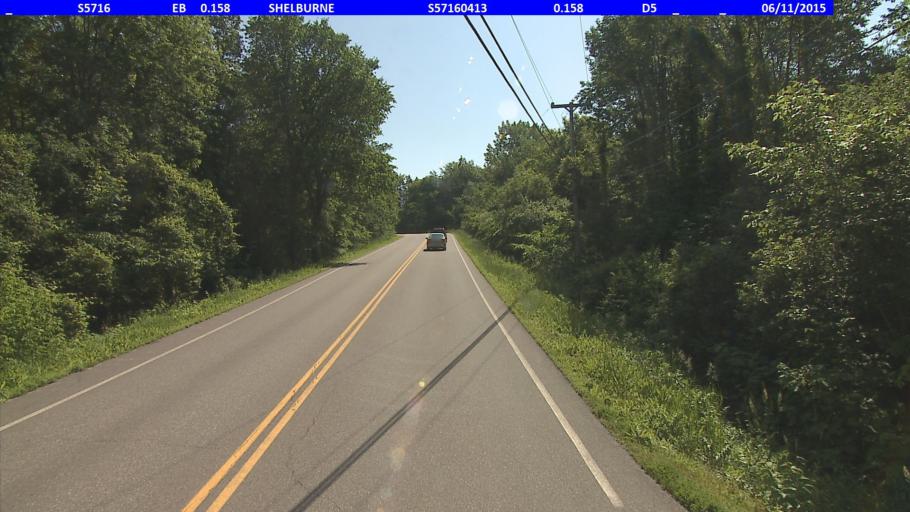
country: US
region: Vermont
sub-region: Chittenden County
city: South Burlington
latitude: 44.3727
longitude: -73.2086
